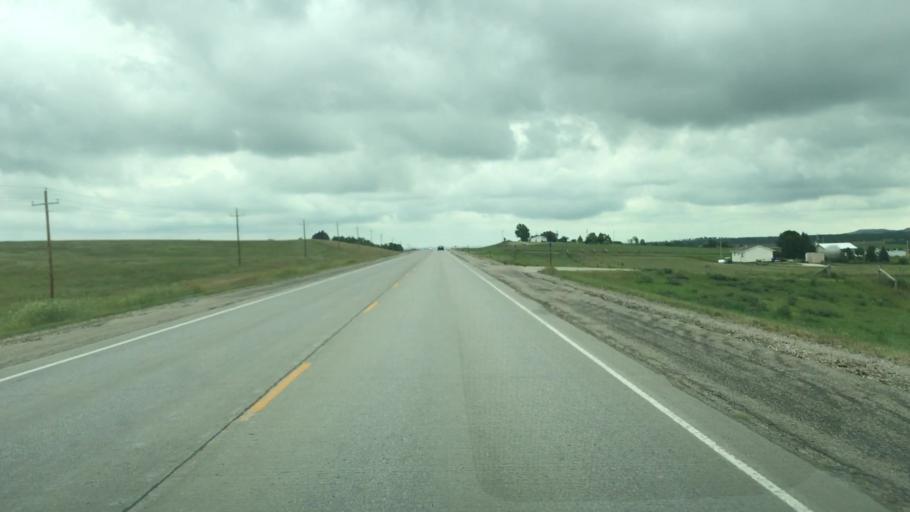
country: US
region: South Dakota
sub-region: Todd County
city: Mission
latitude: 43.3029
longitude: -100.7004
